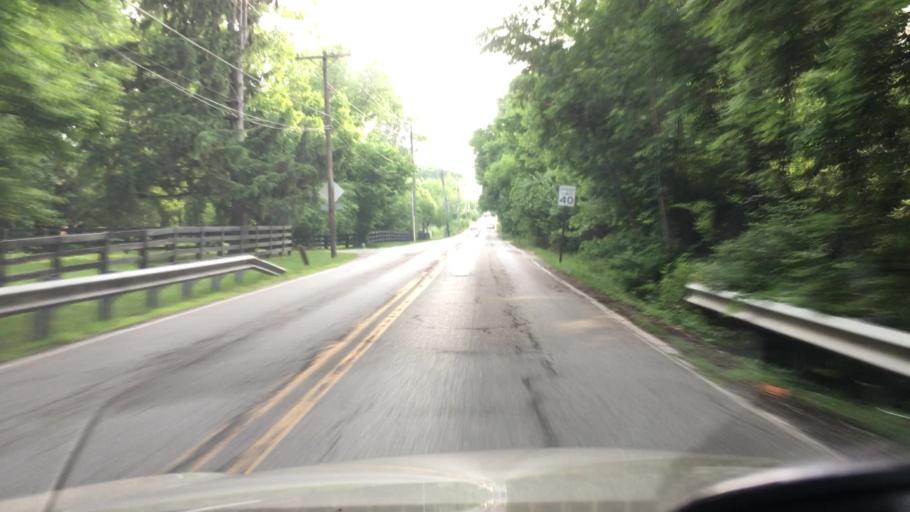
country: US
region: Indiana
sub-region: Marion County
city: Lawrence
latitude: 39.8803
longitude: -86.0148
